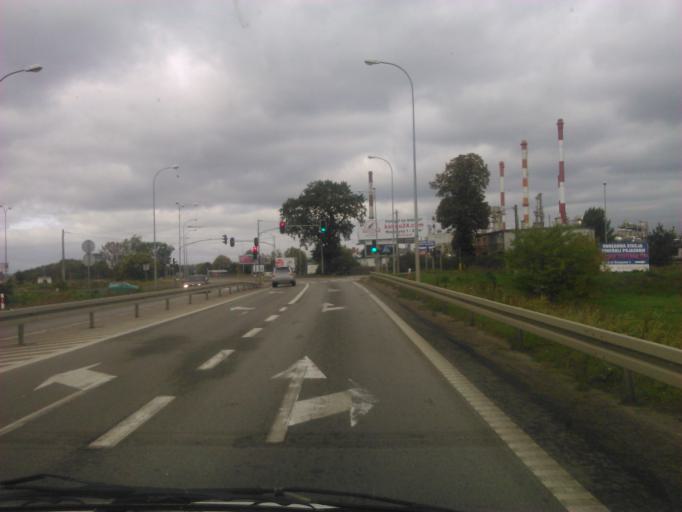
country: PL
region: Pomeranian Voivodeship
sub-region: Gdansk
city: Gdansk
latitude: 54.3381
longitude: 18.7383
